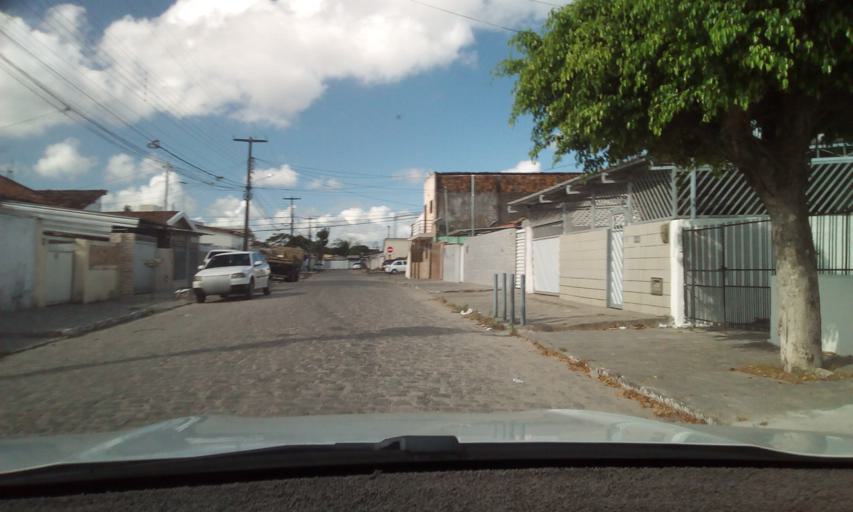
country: BR
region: Paraiba
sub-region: Joao Pessoa
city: Joao Pessoa
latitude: -7.1514
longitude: -34.8926
